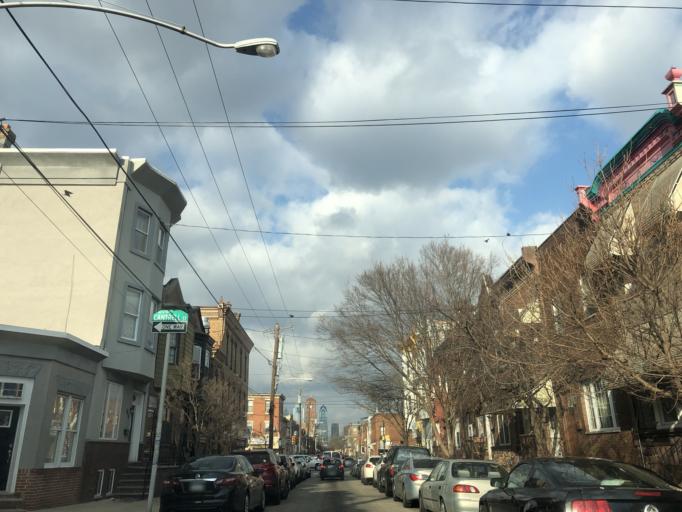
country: US
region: Pennsylvania
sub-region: Philadelphia County
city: Philadelphia
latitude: 39.9242
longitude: -75.1731
